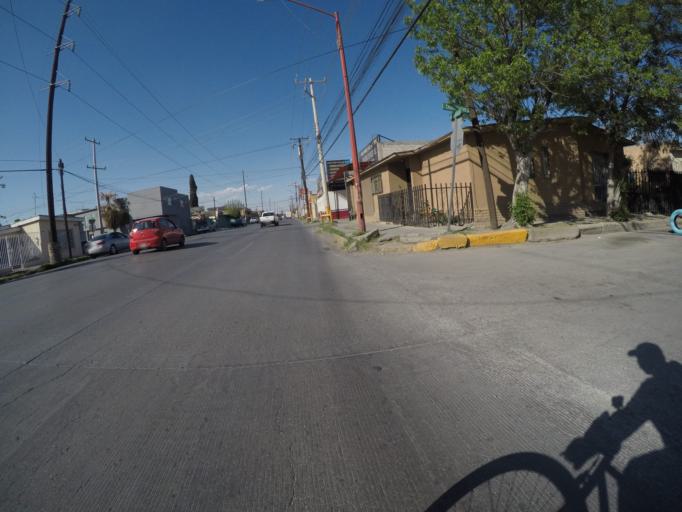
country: MX
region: Chihuahua
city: Ciudad Juarez
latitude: 31.7155
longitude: -106.4449
